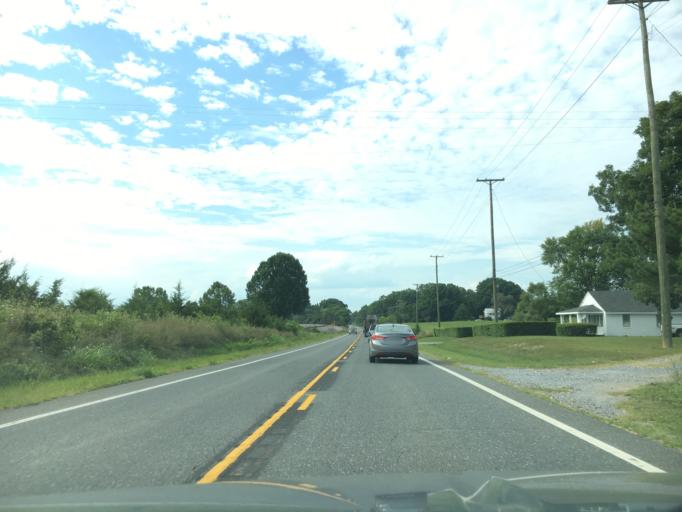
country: US
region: Virginia
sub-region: Campbell County
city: Brookneal
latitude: 37.0810
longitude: -78.9861
